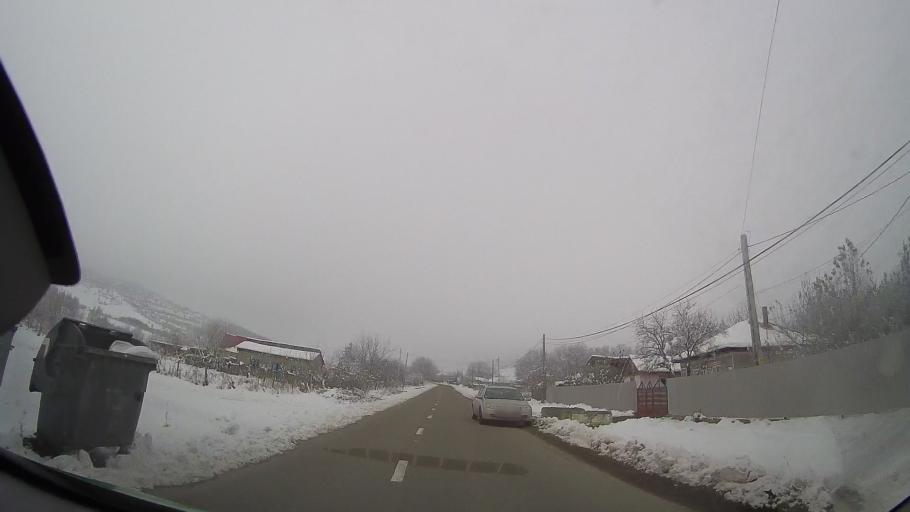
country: RO
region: Neamt
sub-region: Comuna Valea Ursului
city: Valea Ursului
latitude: 46.8009
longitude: 27.1156
